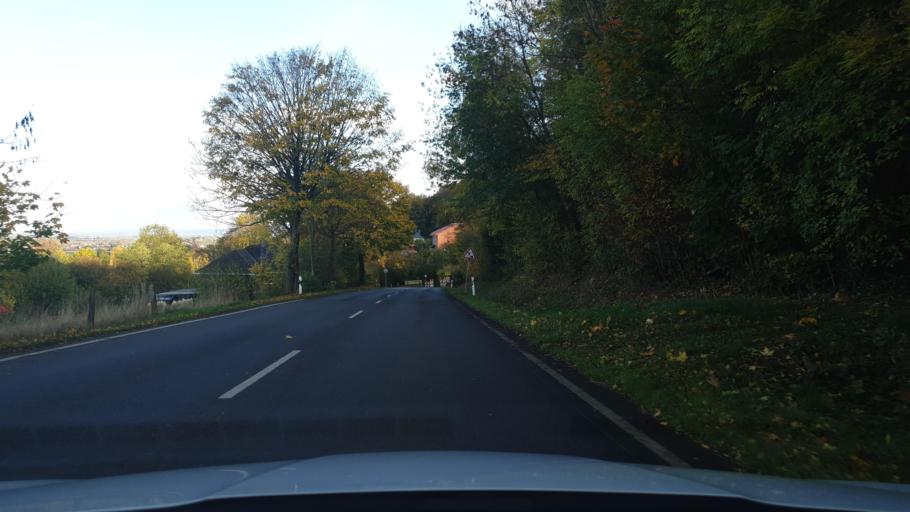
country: DE
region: North Rhine-Westphalia
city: Bad Oeynhausen
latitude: 52.2650
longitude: 8.8059
